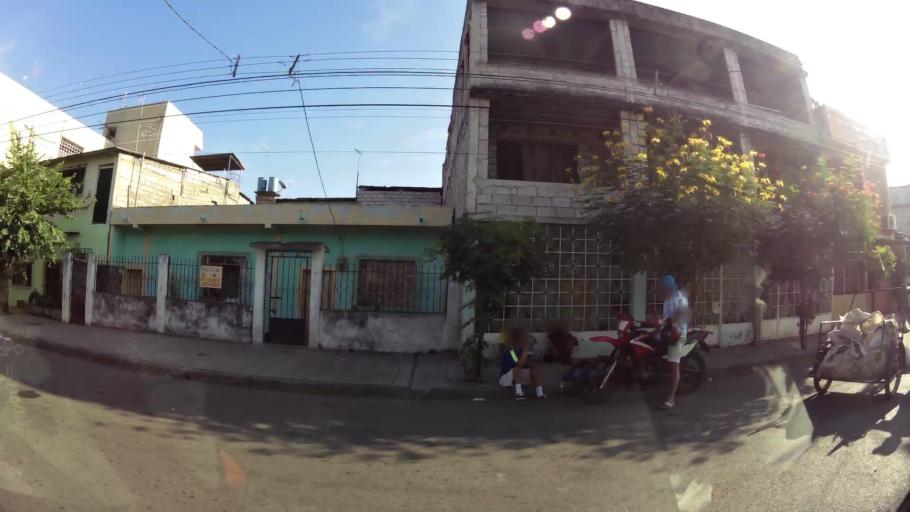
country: EC
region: Guayas
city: Guayaquil
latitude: -2.2177
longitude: -79.9208
